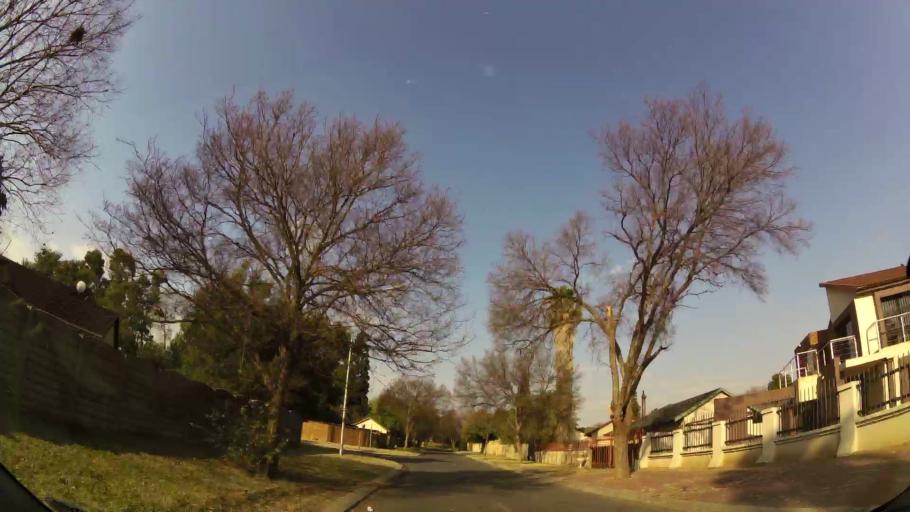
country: ZA
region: Gauteng
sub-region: Ekurhuleni Metropolitan Municipality
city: Benoni
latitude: -26.1334
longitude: 28.3643
